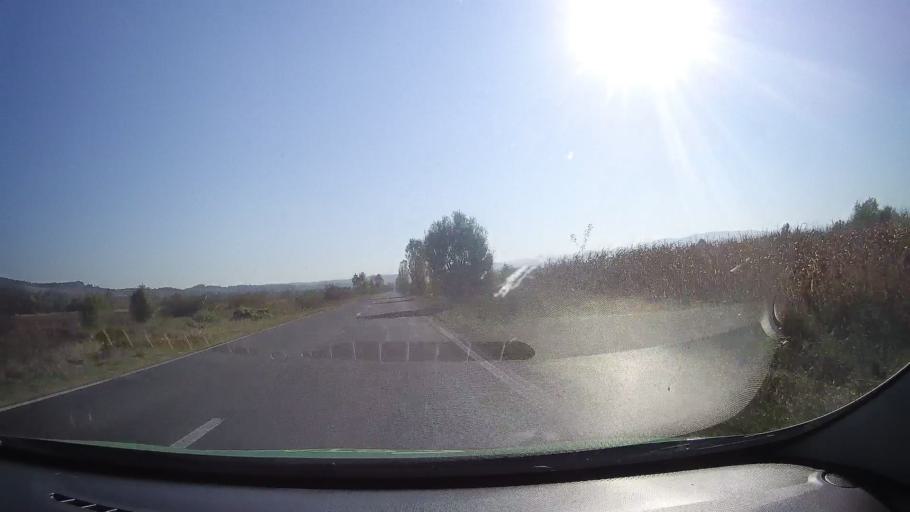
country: RO
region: Timis
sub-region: Comuna Margina
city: Margina
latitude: 45.8541
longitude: 22.2835
